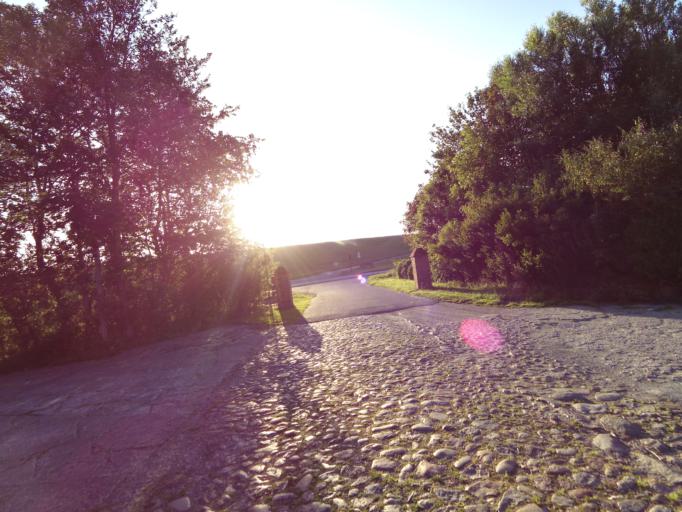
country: DE
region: Lower Saxony
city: Cappel
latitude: 53.7684
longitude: 8.5457
